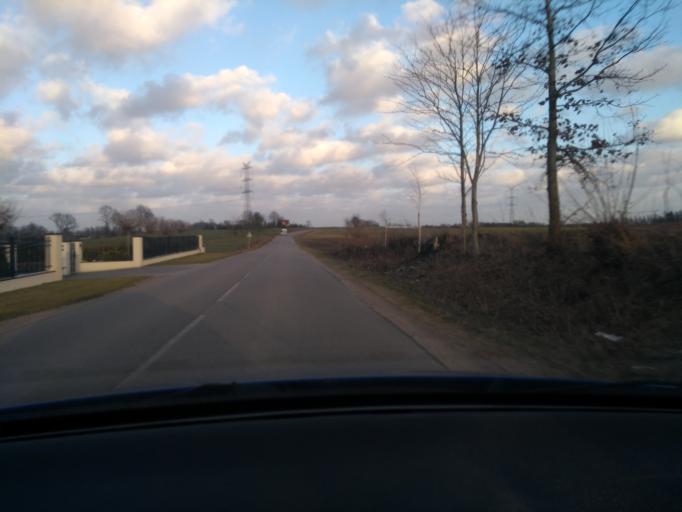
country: PL
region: Pomeranian Voivodeship
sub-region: Powiat kartuski
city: Przodkowo
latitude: 54.4171
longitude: 18.2899
